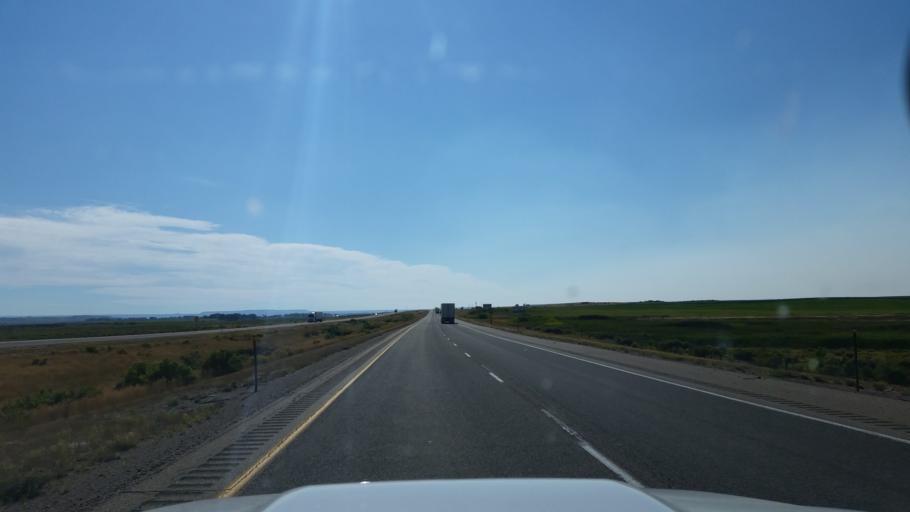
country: US
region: Wyoming
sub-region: Uinta County
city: Lyman
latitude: 41.3743
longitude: -110.2472
